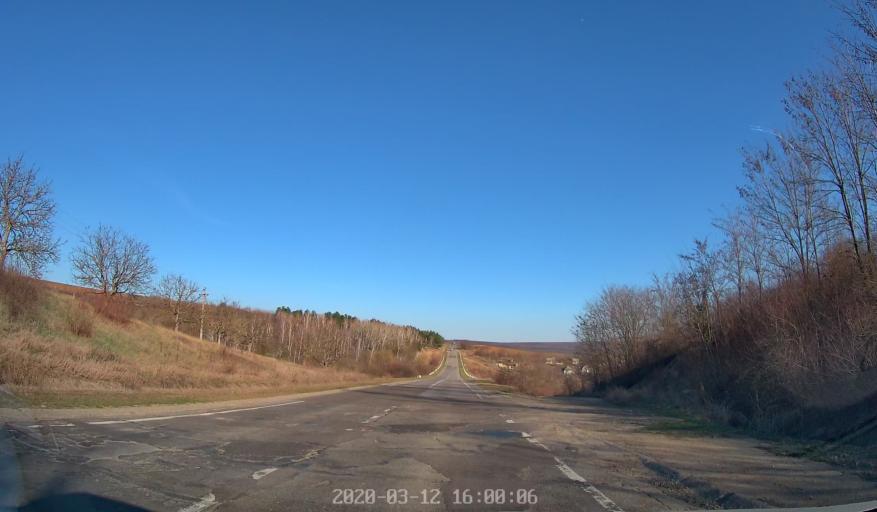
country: MD
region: Chisinau
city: Vadul lui Voda
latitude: 47.0439
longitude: 29.1003
